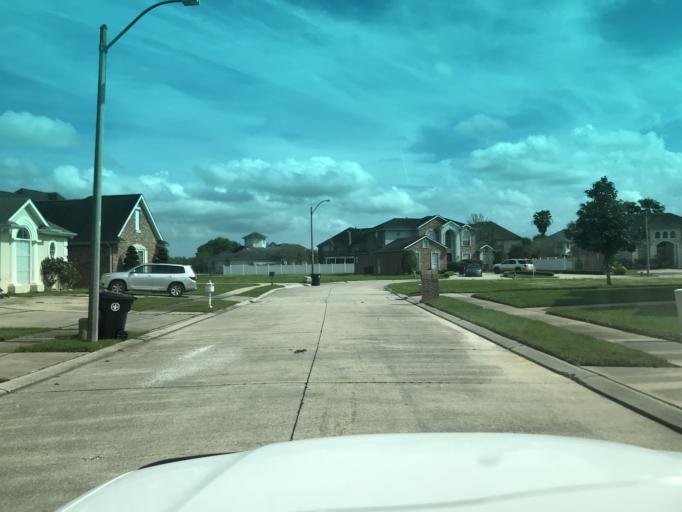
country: US
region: Louisiana
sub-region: Saint Bernard Parish
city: Chalmette
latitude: 30.0368
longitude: -89.9506
